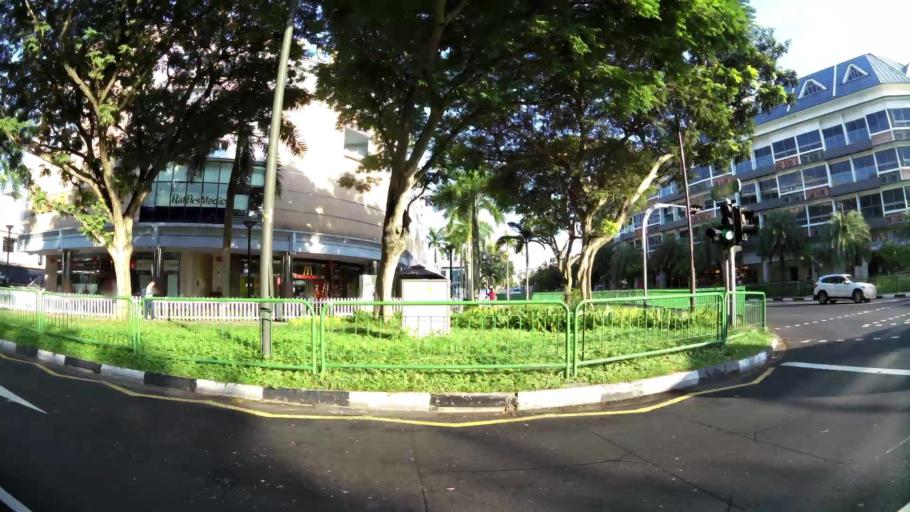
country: SG
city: Singapore
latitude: 1.3123
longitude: 103.9235
